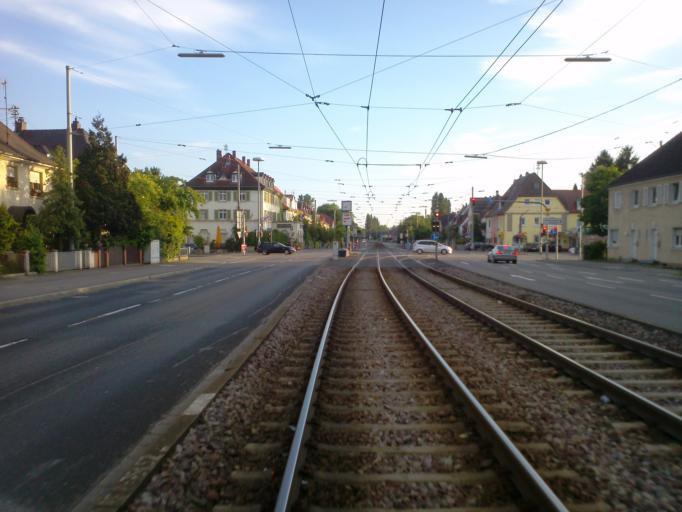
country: DE
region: Baden-Wuerttemberg
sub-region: Karlsruhe Region
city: Karlsruhe
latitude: 49.0062
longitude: 8.3511
